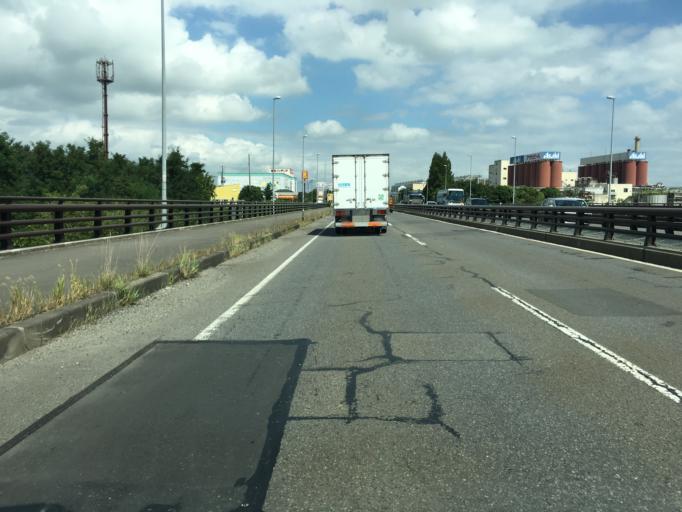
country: JP
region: Fukushima
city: Motomiya
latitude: 37.4759
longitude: 140.3785
